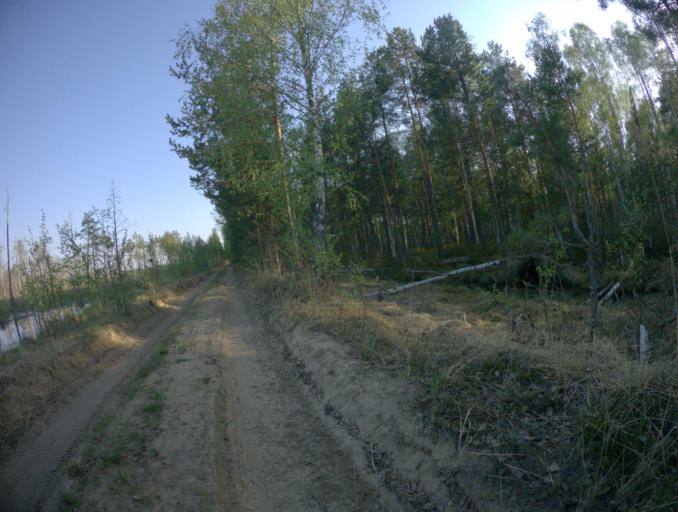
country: RU
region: Vladimir
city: Vyazniki
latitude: 56.3887
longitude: 42.1724
